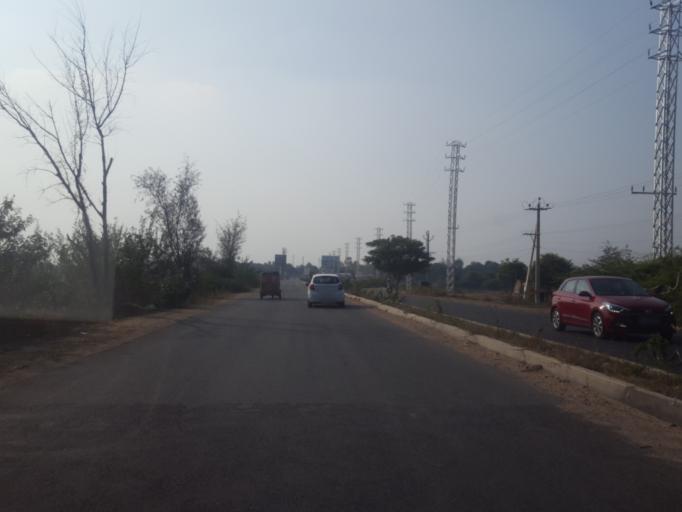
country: IN
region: Telangana
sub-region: Medak
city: Serilingampalle
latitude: 17.3971
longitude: 78.3069
